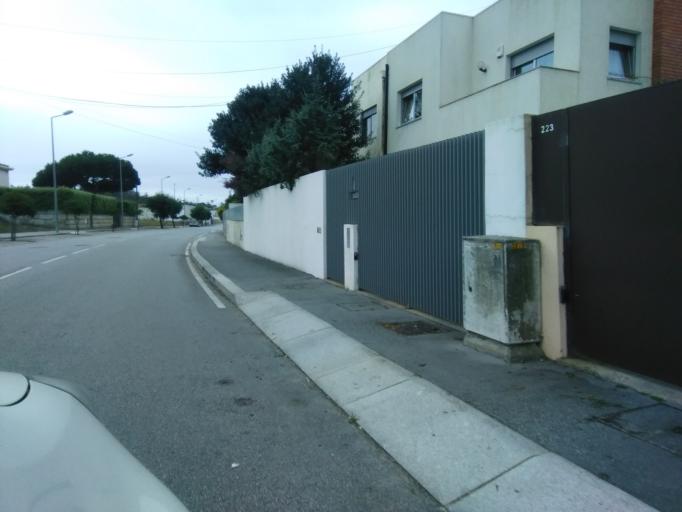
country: PT
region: Porto
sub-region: Matosinhos
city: Lavra
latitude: 41.2501
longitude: -8.7189
